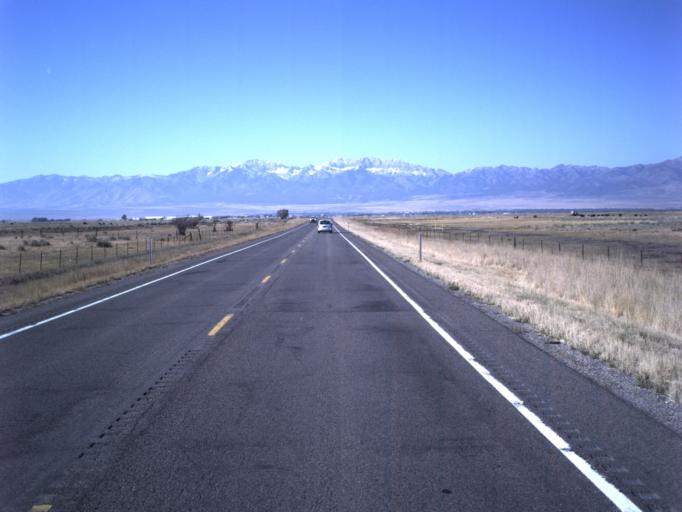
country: US
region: Utah
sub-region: Tooele County
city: Erda
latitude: 40.6297
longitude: -112.3412
